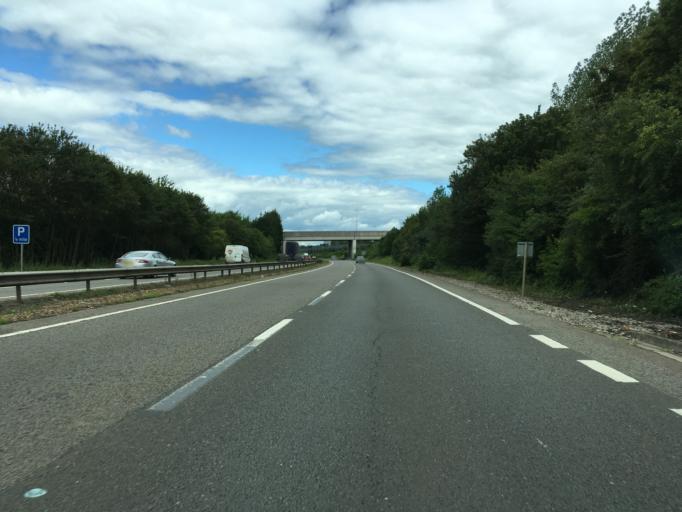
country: GB
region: England
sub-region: Milton Keynes
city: Milton Keynes
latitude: 52.0214
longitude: -0.7595
